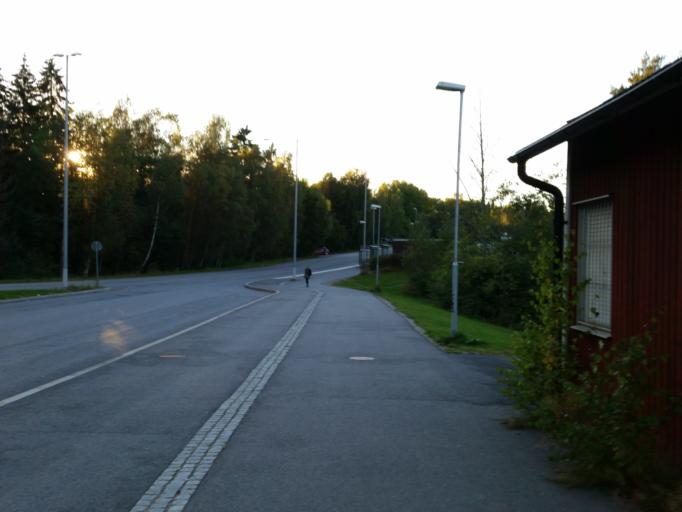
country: SE
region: Stockholm
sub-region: Haninge Kommun
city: Haninge
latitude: 59.1688
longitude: 18.1993
